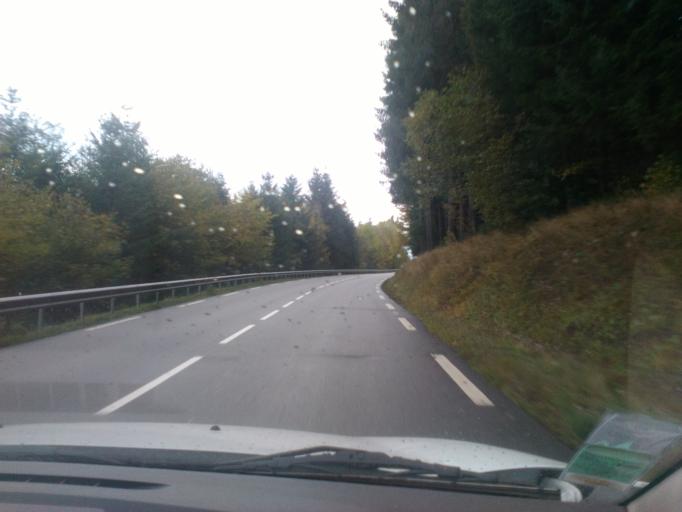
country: FR
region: Lorraine
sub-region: Departement des Vosges
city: Xonrupt-Longemer
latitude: 48.1179
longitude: 6.9105
